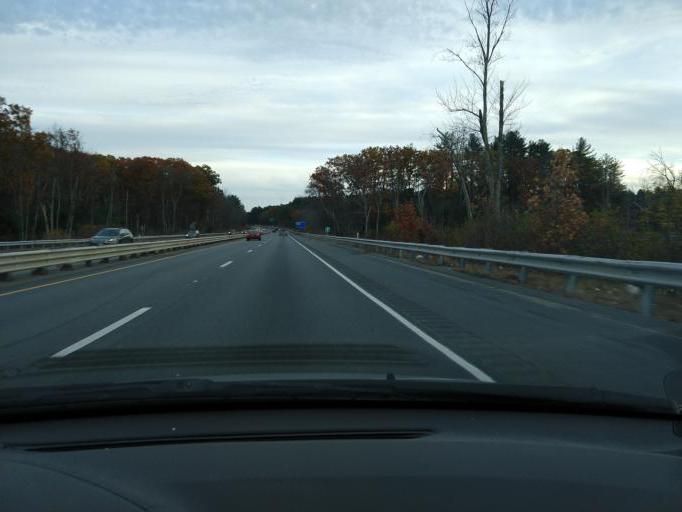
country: US
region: Massachusetts
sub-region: Middlesex County
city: Littleton Common
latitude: 42.5095
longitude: -71.4896
